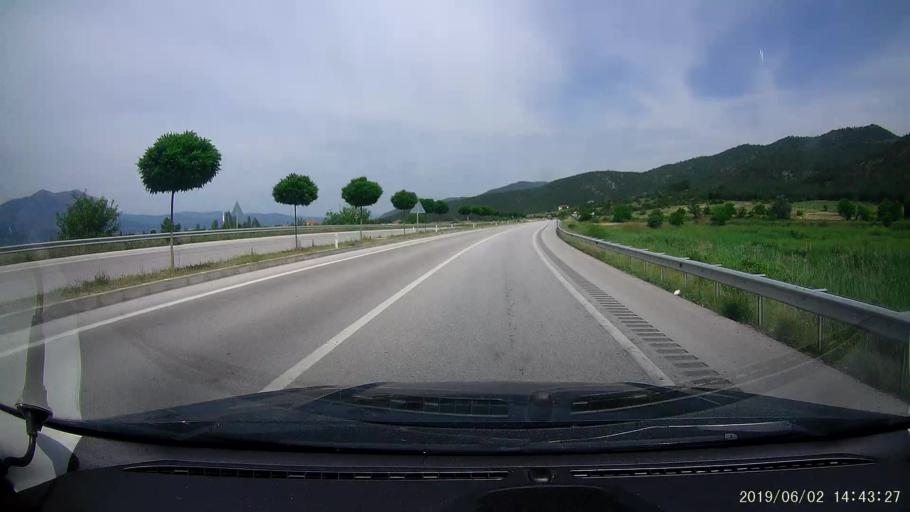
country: TR
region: Corum
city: Hacihamza
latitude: 41.0986
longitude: 34.3866
